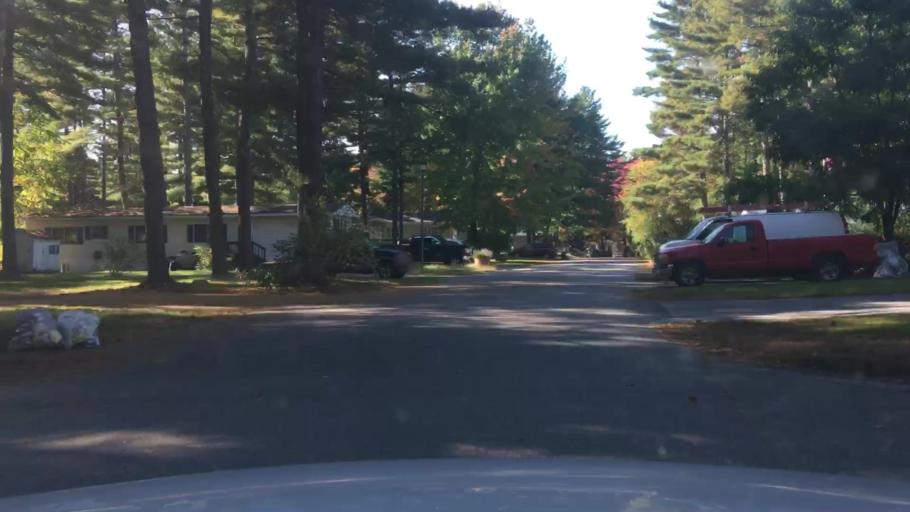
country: US
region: Maine
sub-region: Cumberland County
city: Gorham
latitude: 43.6238
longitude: -70.4511
